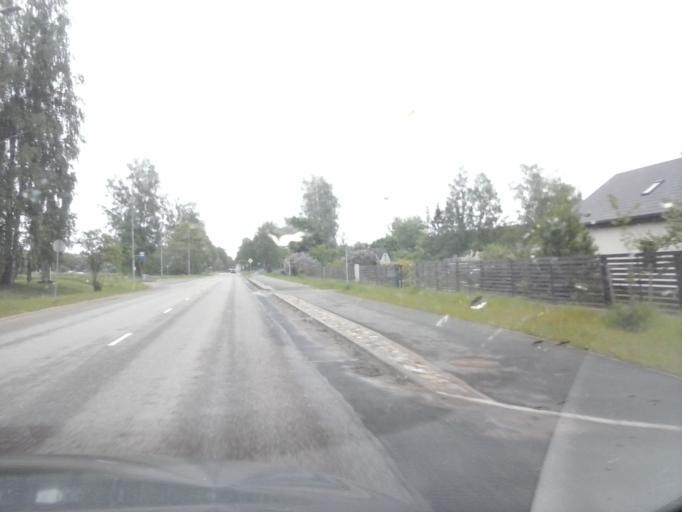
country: LV
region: Valmieras Rajons
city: Valmiera
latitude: 57.5527
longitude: 25.4362
